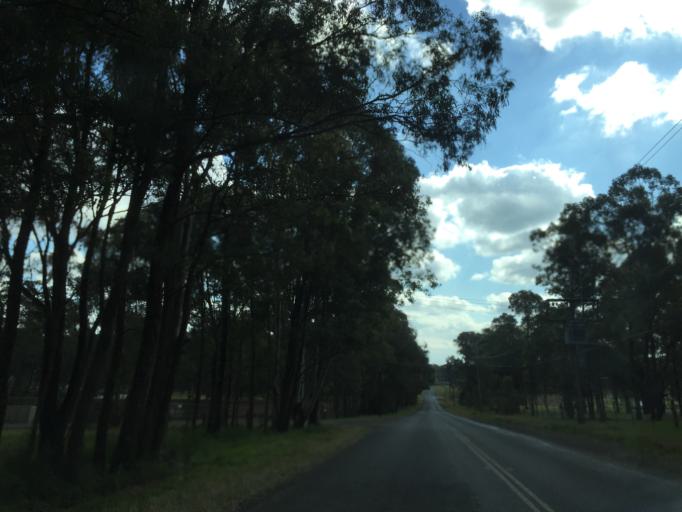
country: AU
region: New South Wales
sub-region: Blacktown
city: Rouse Hill
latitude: -33.6811
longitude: 150.9072
